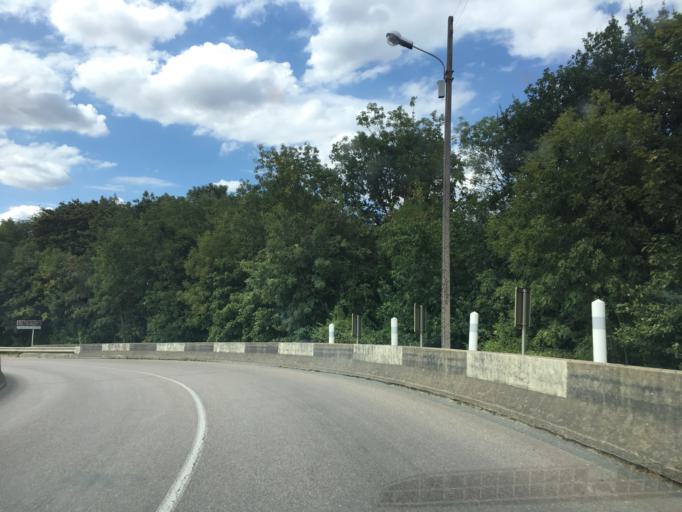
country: FR
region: Bourgogne
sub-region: Departement de l'Yonne
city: Joigny
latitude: 47.9742
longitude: 3.3974
